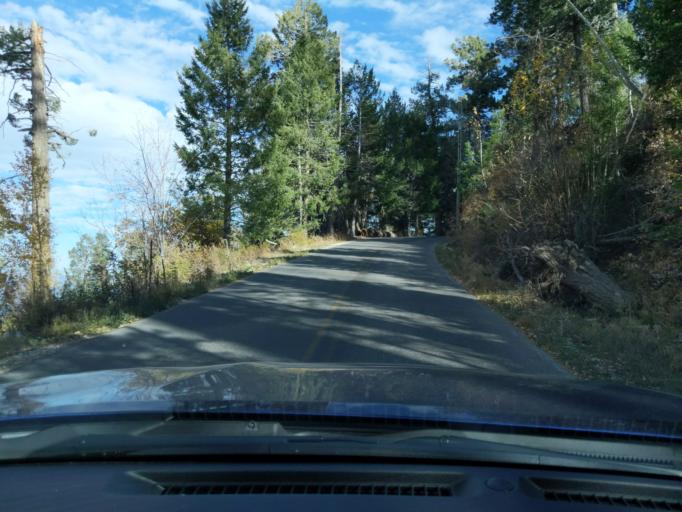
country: US
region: Arizona
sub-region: Pima County
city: Catalina
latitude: 32.4447
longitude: -110.7874
